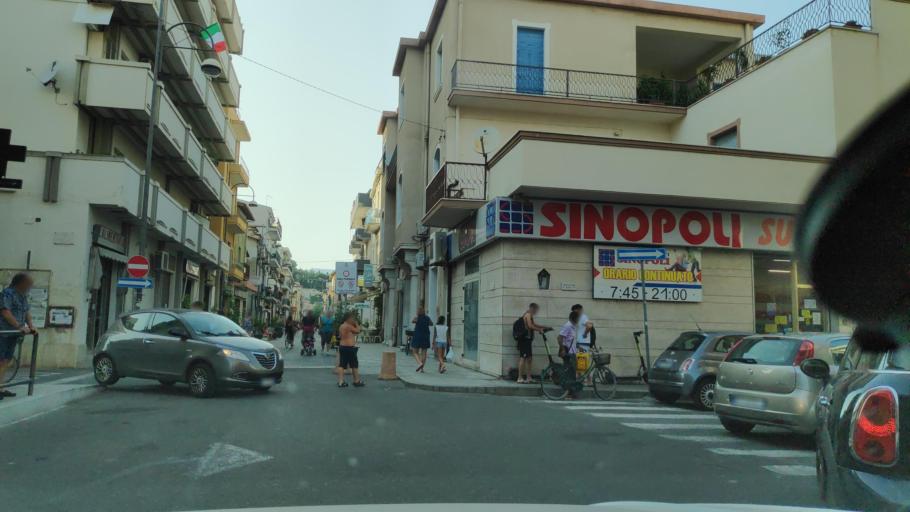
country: IT
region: Calabria
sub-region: Provincia di Catanzaro
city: Soverato Marina
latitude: 38.6883
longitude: 16.5484
